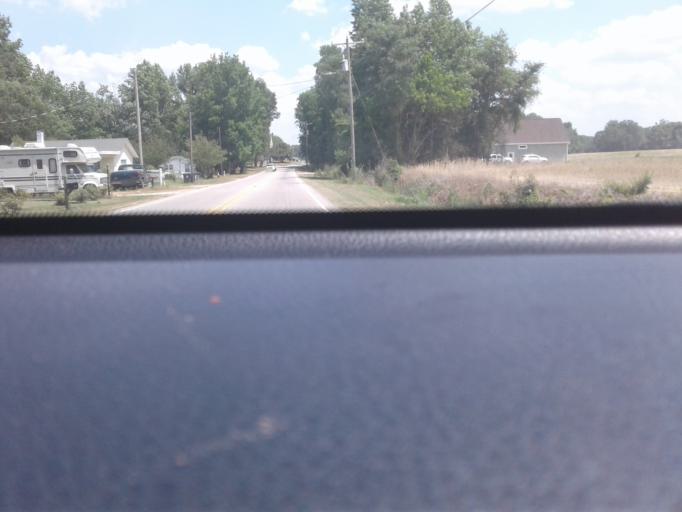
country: US
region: North Carolina
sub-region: Harnett County
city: Erwin
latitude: 35.3133
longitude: -78.6787
